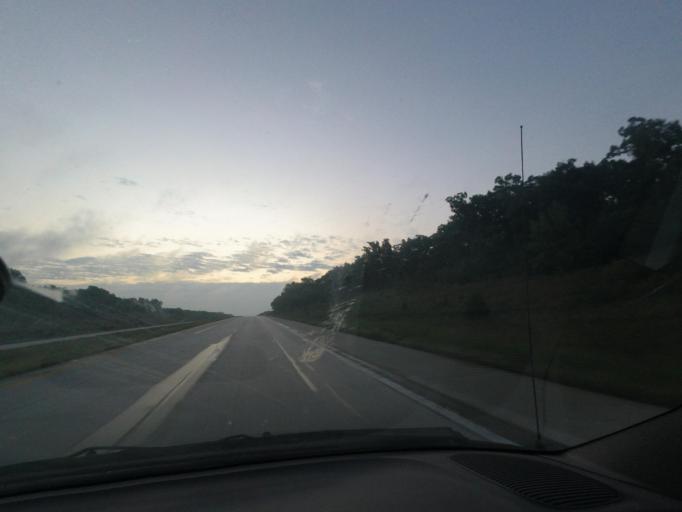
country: US
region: Missouri
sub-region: Linn County
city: Marceline
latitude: 39.7590
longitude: -92.8492
